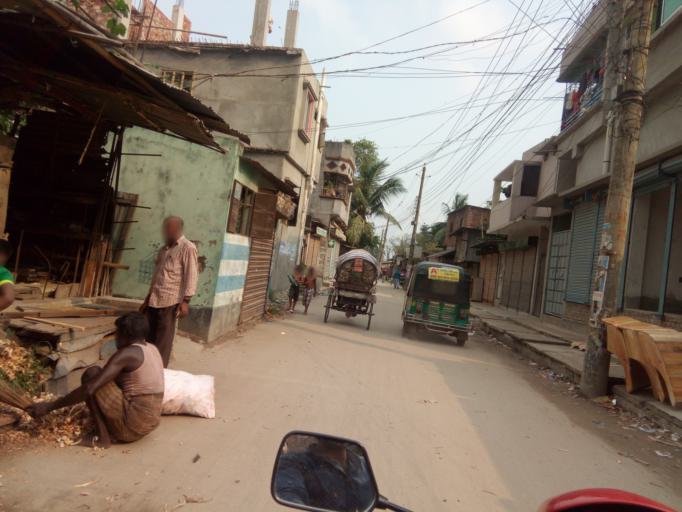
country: BD
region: Dhaka
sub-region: Dhaka
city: Dhaka
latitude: 23.7101
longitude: 90.4576
